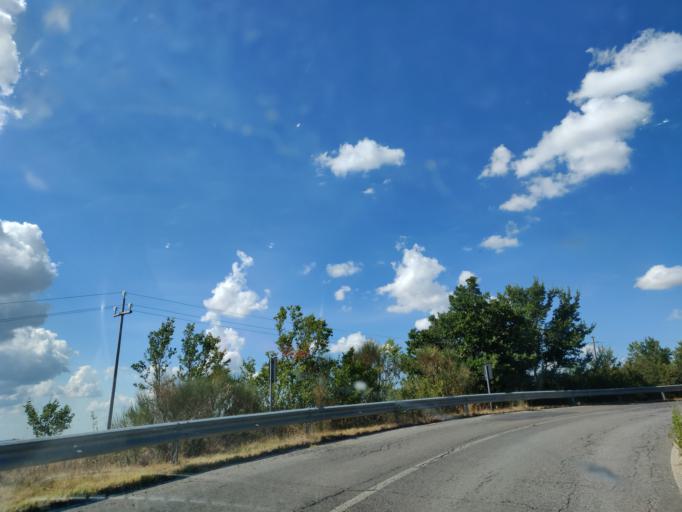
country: IT
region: Tuscany
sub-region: Provincia di Siena
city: Radicofani
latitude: 42.9403
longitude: 11.7331
